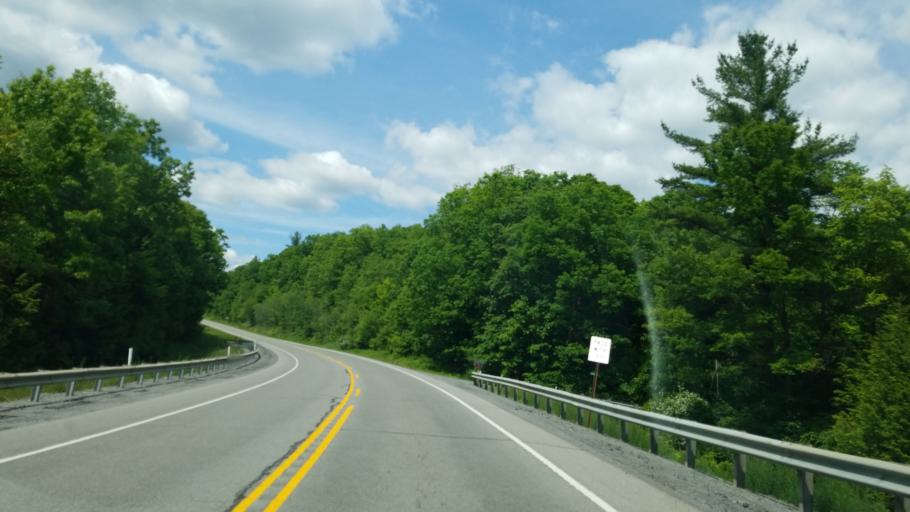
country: US
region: Pennsylvania
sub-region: Clearfield County
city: Clearfield
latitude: 40.9598
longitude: -78.3686
